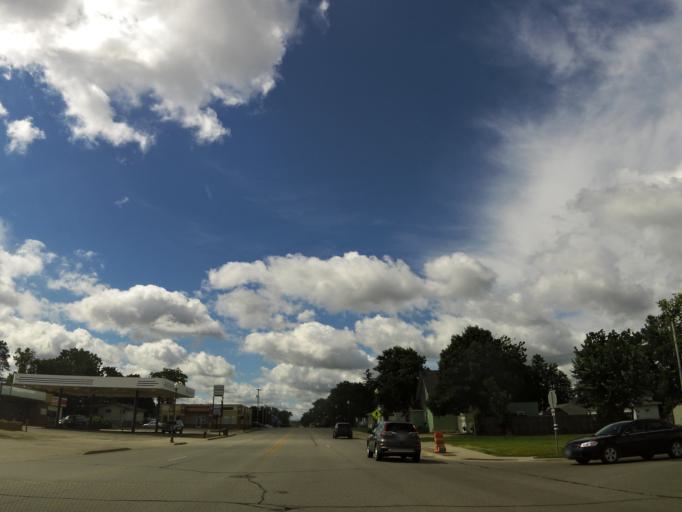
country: US
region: Minnesota
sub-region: Olmsted County
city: Stewartville
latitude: 43.8539
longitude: -92.4886
